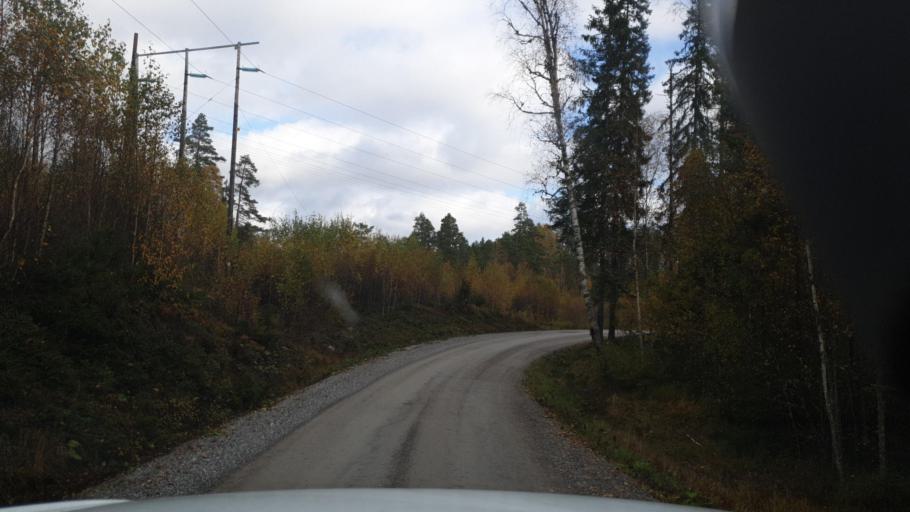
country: SE
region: Vaermland
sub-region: Arvika Kommun
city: Arvika
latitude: 59.5352
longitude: 12.3980
